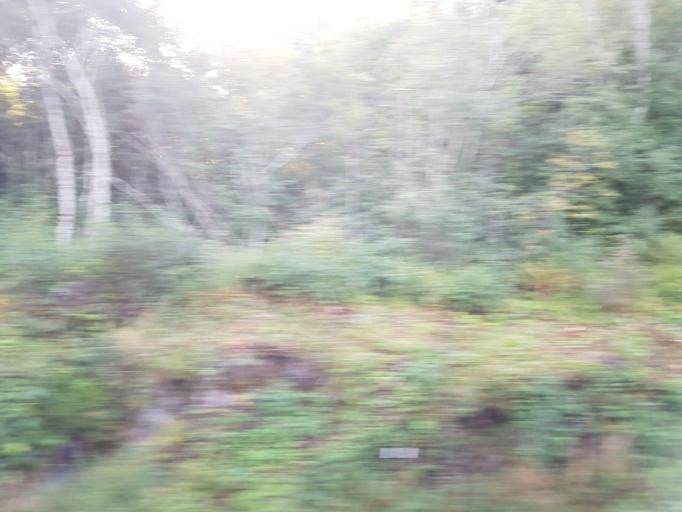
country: NO
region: Sor-Trondelag
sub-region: Trondheim
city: Trondheim
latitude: 63.4517
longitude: 10.2427
